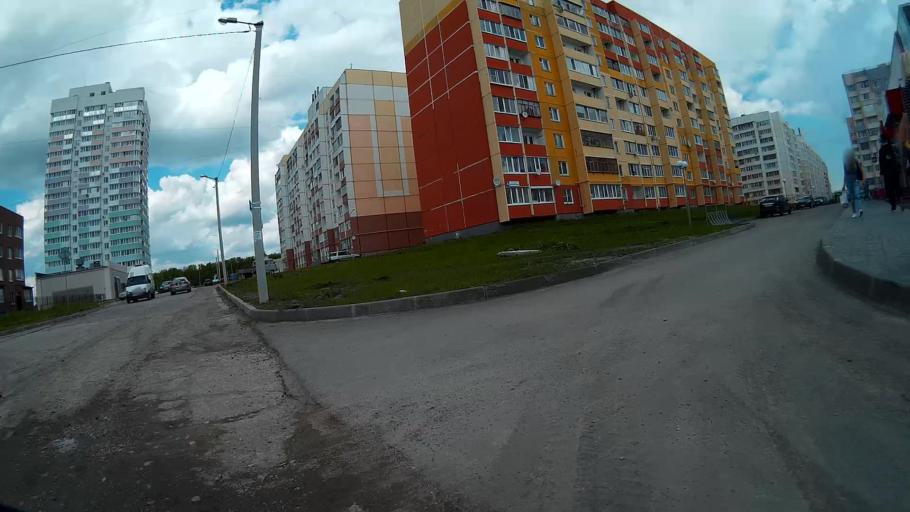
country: RU
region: Ulyanovsk
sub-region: Ulyanovskiy Rayon
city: Ulyanovsk
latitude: 54.3483
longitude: 48.3423
